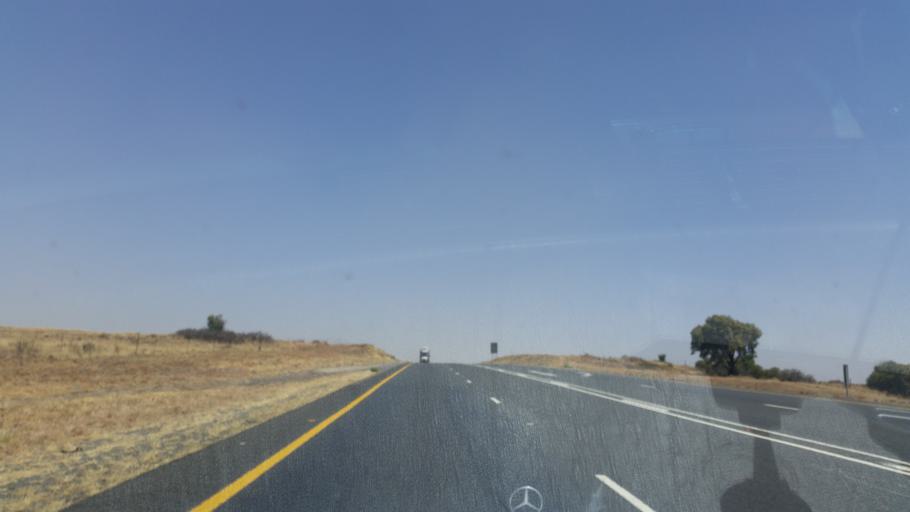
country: ZA
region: Orange Free State
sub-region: Lejweleputswa District Municipality
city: Winburg
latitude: -28.6899
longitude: 26.8156
